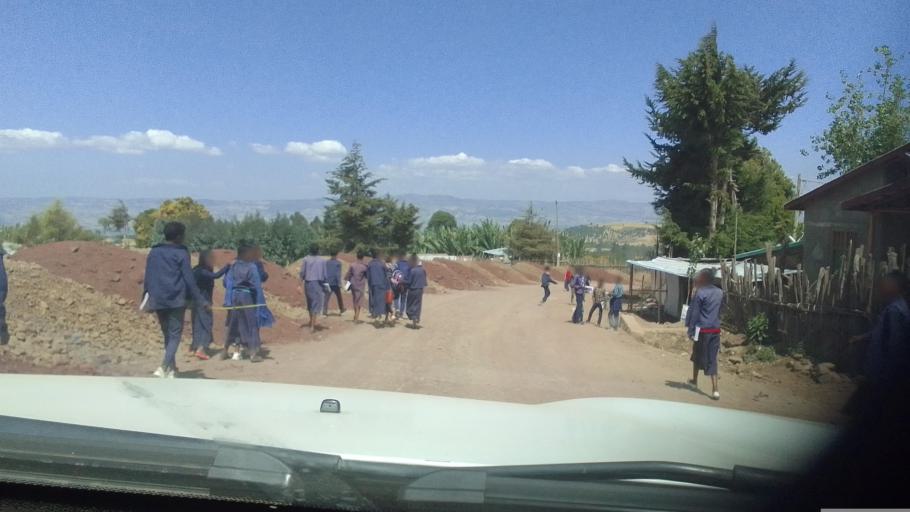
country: ET
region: Oromiya
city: Hagere Hiywet
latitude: 8.8620
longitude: 37.8903
